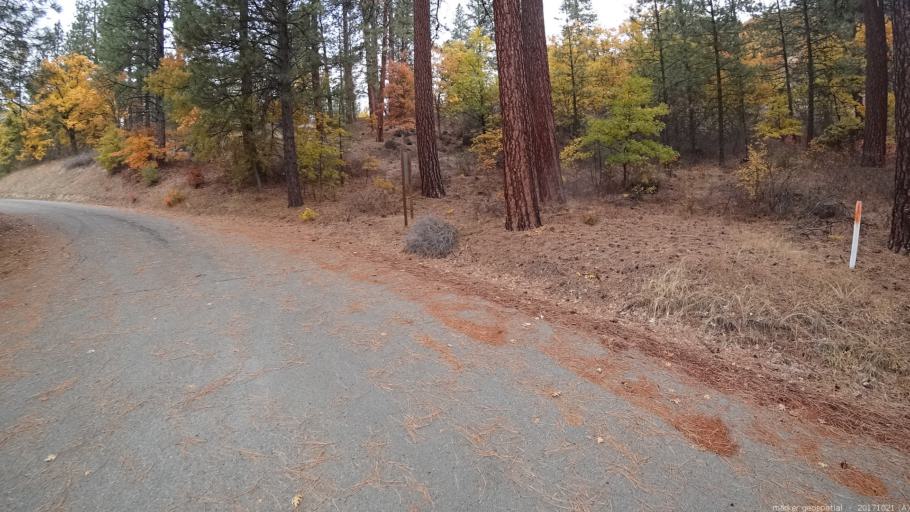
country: US
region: California
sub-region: Shasta County
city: Burney
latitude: 41.0220
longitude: -121.6239
